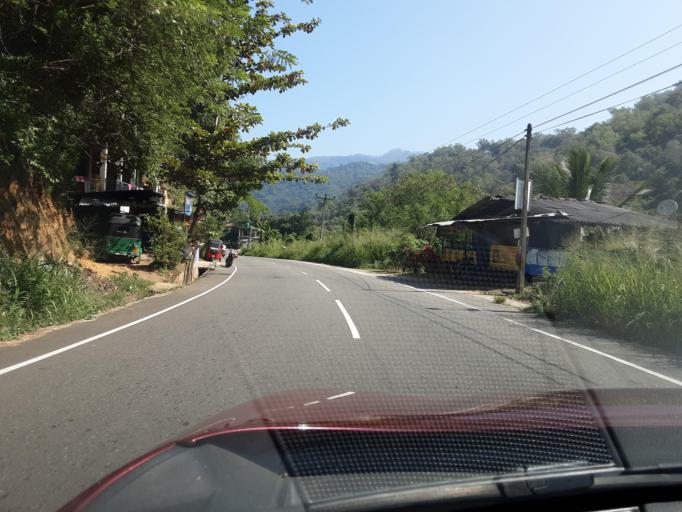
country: LK
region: Uva
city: Badulla
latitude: 7.0362
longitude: 81.0586
